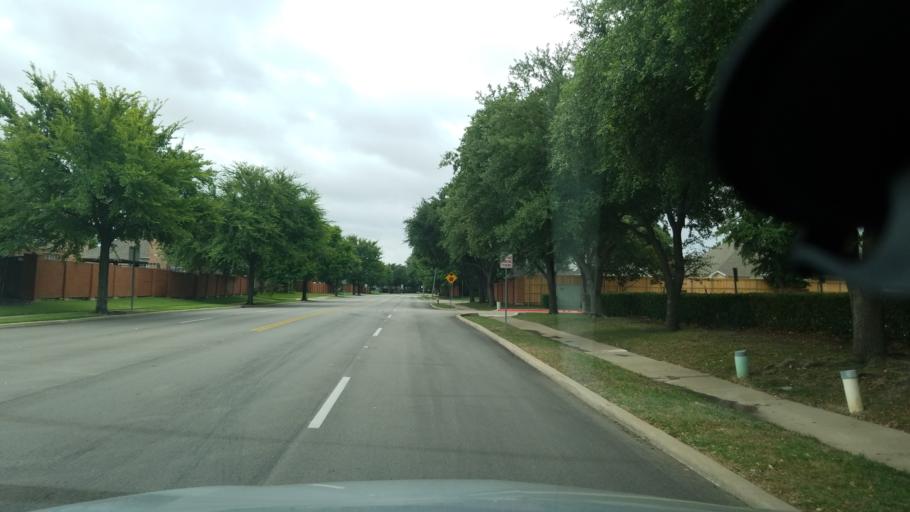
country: US
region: Texas
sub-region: Dallas County
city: Farmers Branch
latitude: 32.9433
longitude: -96.9447
